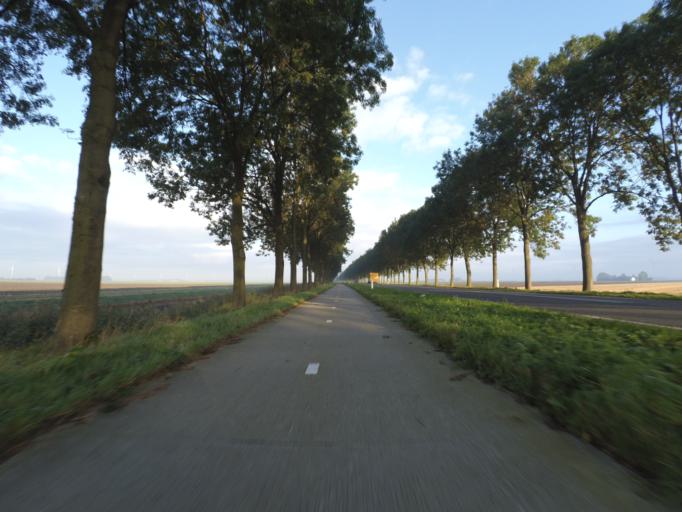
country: NL
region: Flevoland
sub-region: Gemeente Dronten
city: Biddinghuizen
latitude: 52.4637
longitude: 5.6883
